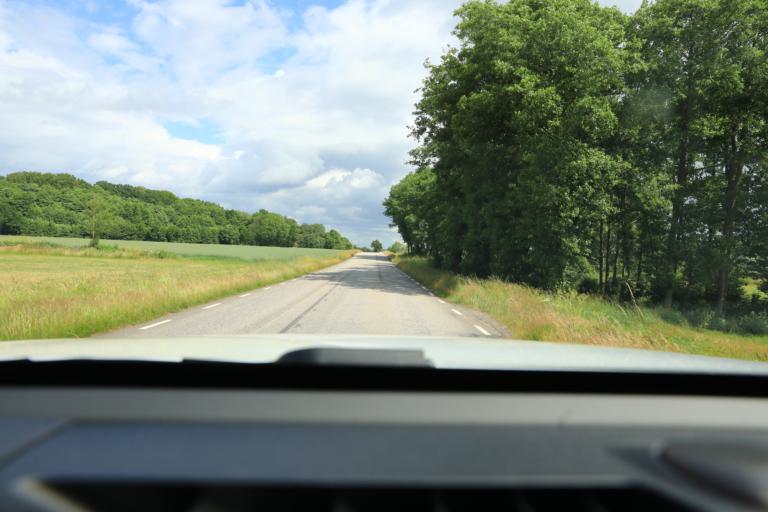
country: SE
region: Halland
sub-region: Varbergs Kommun
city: Tvaaker
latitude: 57.0849
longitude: 12.4027
